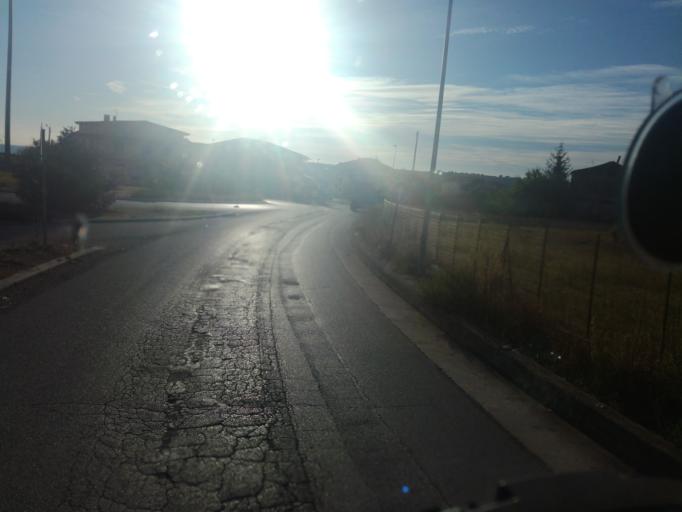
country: IT
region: Abruzzo
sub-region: Provincia di Chieti
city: Francavilla al Mare
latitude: 42.3981
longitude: 14.2930
